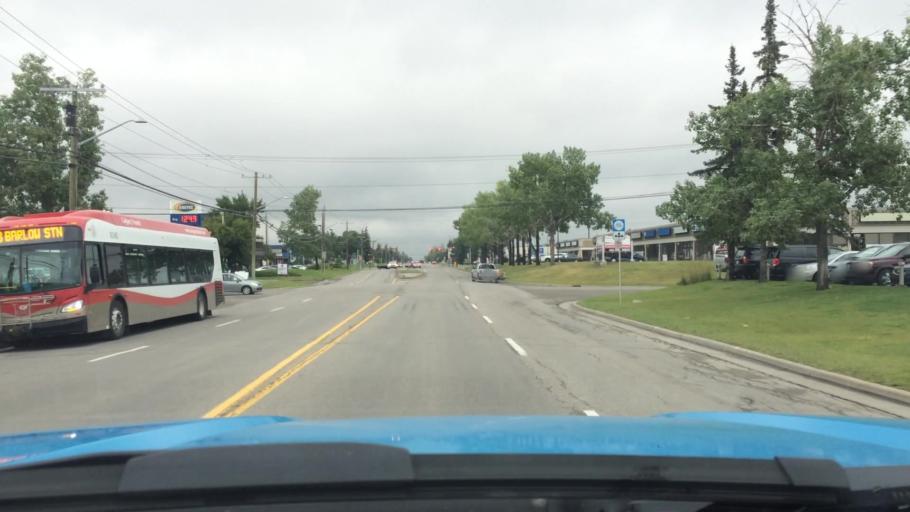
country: CA
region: Alberta
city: Calgary
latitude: 51.0791
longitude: -114.0116
